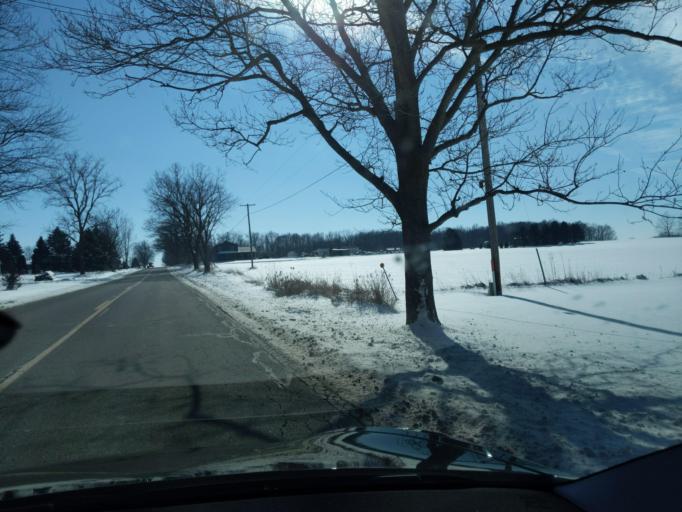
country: US
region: Michigan
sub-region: Livingston County
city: Fowlerville
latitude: 42.6250
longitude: -84.0717
